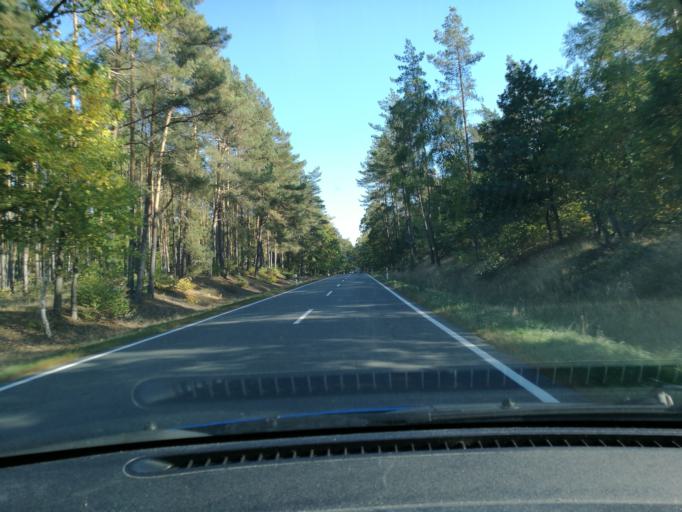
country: DE
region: Lower Saxony
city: Gohrde
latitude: 53.1490
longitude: 10.8548
